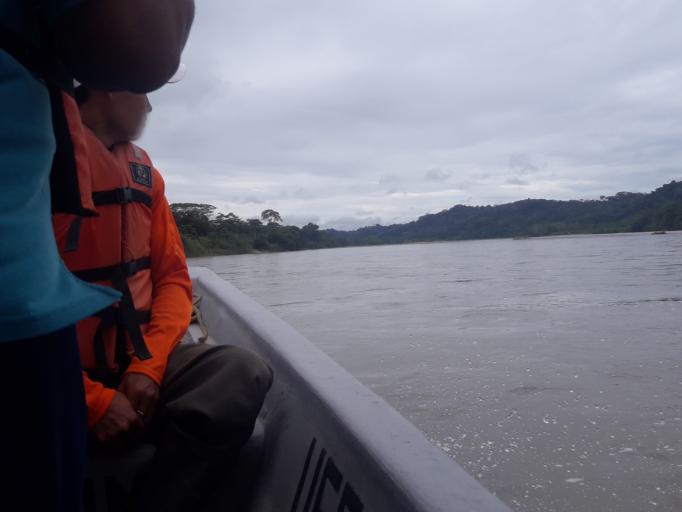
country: EC
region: Orellana
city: Boca Suno
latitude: -0.8793
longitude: -77.2893
